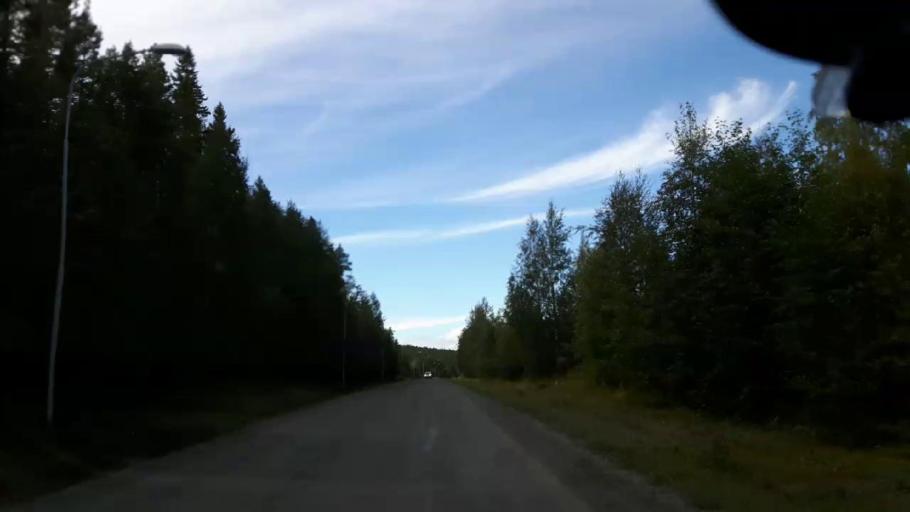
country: SE
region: Jaemtland
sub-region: Ragunda Kommun
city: Hammarstrand
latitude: 63.1409
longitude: 15.9189
